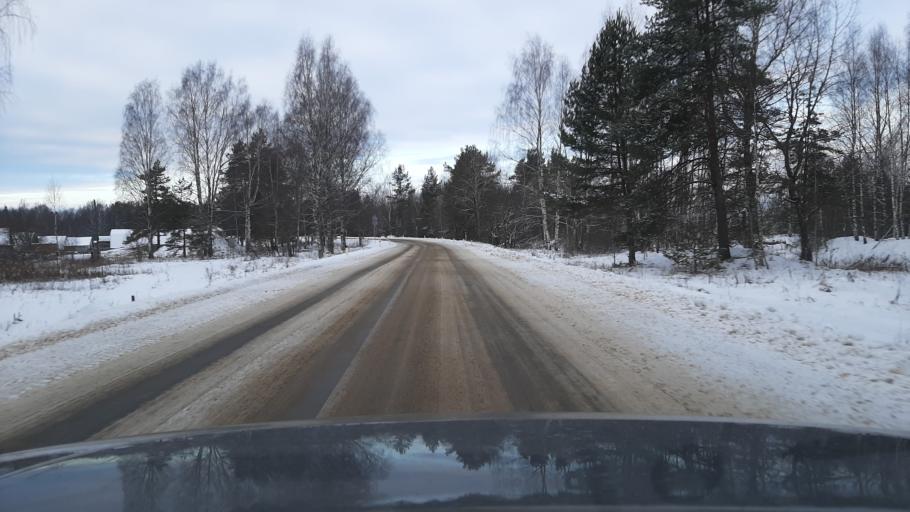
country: RU
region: Kostroma
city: Nerekhta
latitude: 57.4714
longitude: 40.6416
